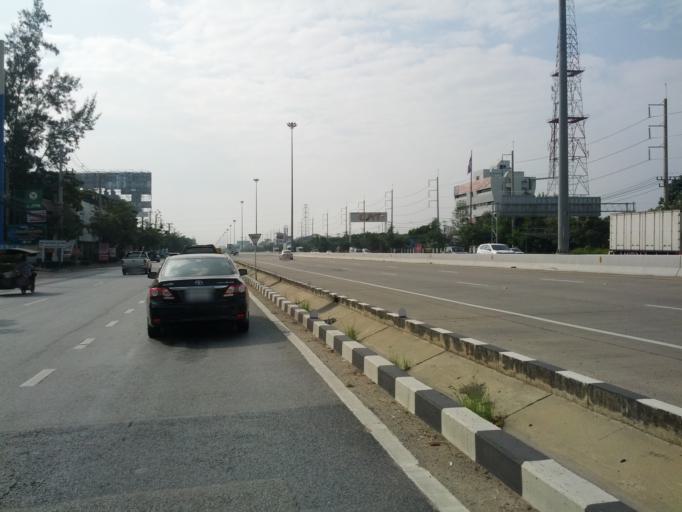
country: TH
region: Chiang Mai
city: Chiang Mai
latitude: 18.7797
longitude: 99.0275
